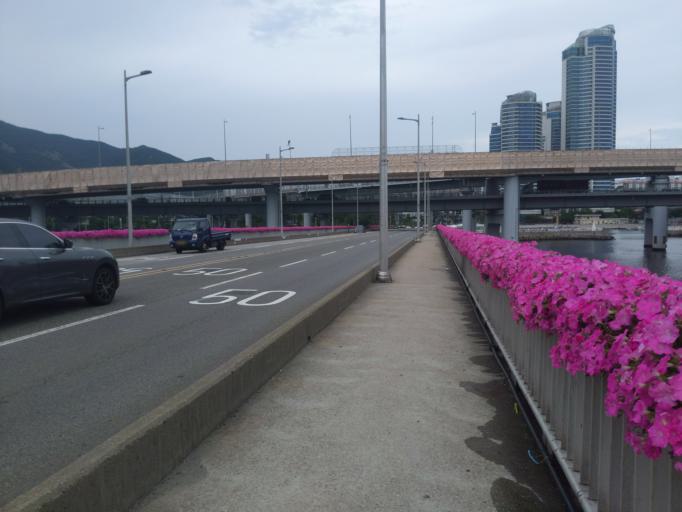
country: KR
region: Busan
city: Busan
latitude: 35.1613
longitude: 129.1316
